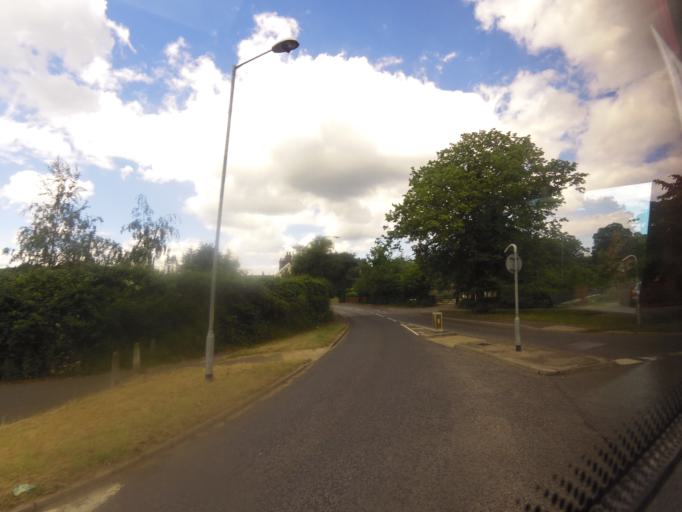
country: GB
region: England
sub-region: Norfolk
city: Cromer
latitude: 52.8845
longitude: 1.2978
